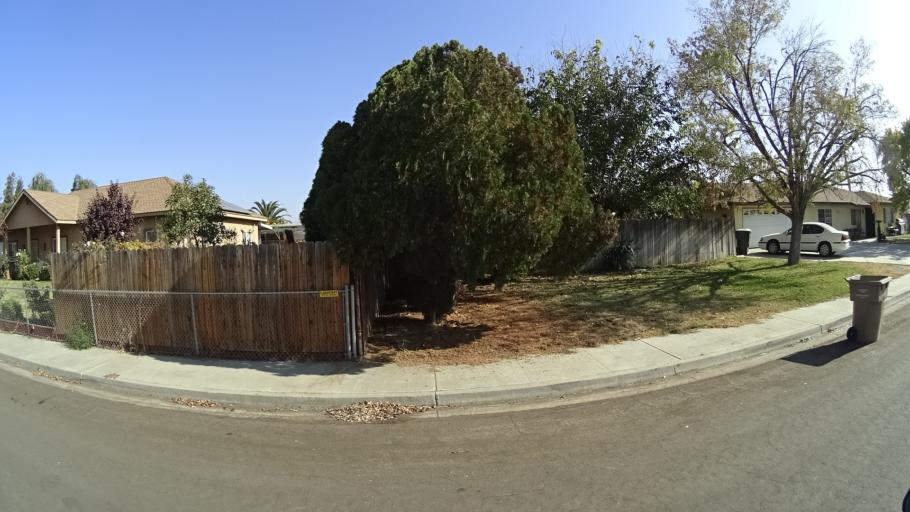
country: US
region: California
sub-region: Kern County
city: Greenfield
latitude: 35.2747
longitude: -119.0155
